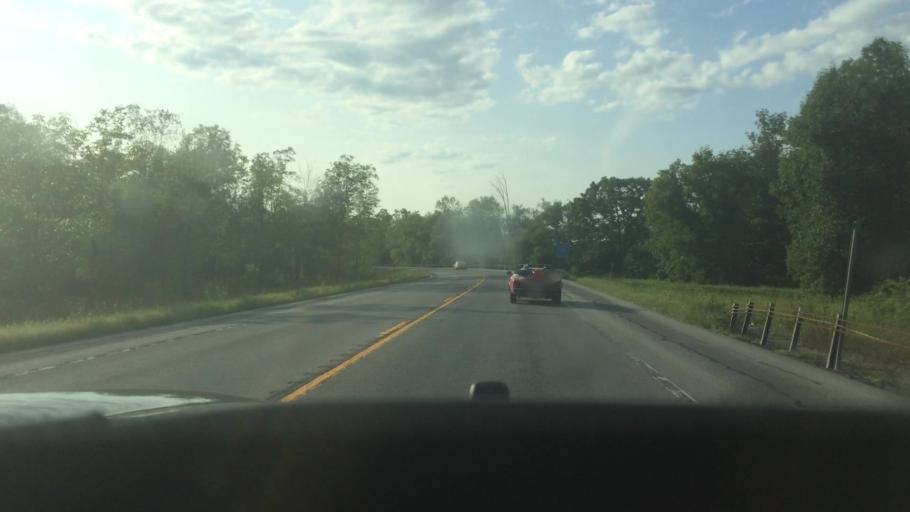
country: US
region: New York
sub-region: St. Lawrence County
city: Canton
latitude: 44.6179
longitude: -75.2222
